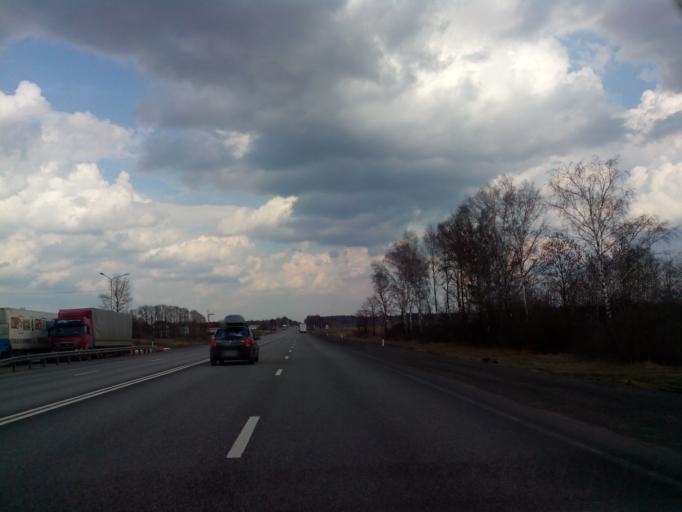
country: RU
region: Moskovskaya
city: Dorokhovo
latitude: 55.5078
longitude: 36.2381
